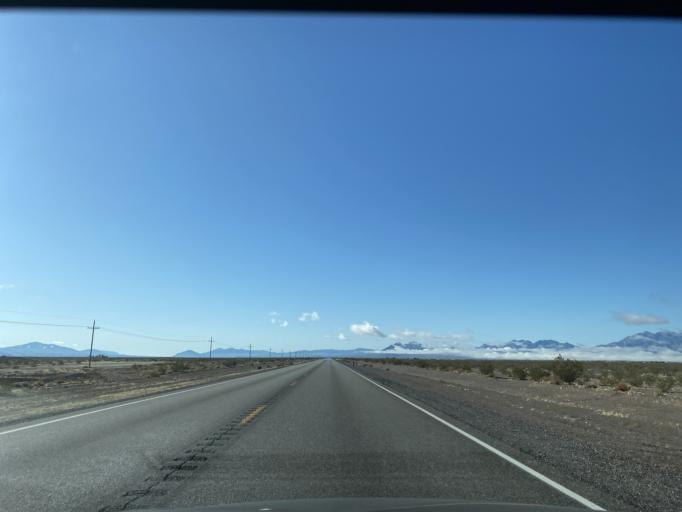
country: US
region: Nevada
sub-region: Nye County
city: Beatty
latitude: 36.5922
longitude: -116.4095
